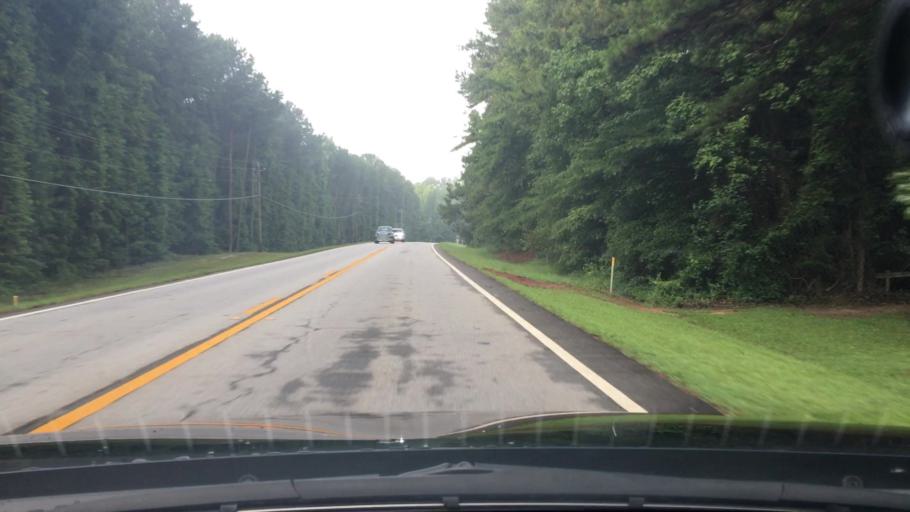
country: US
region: Georgia
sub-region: Fayette County
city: Peachtree City
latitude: 33.3565
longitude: -84.6359
